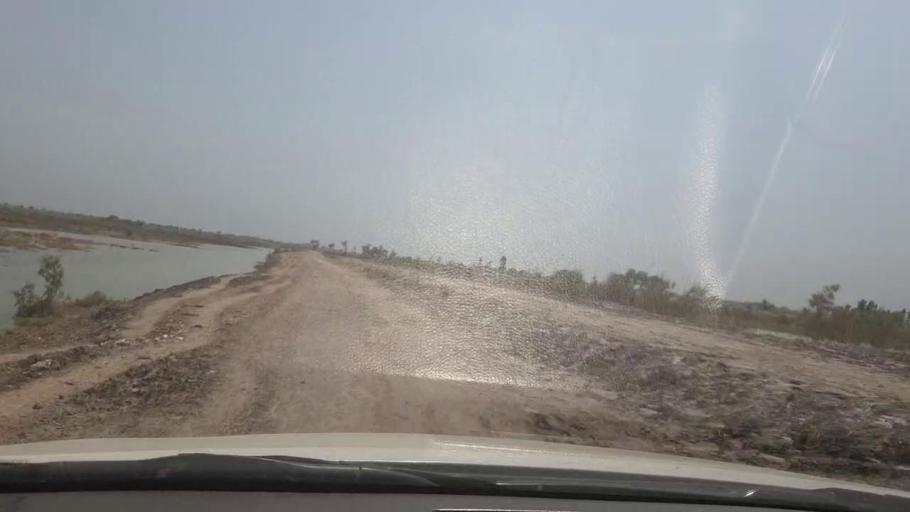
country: PK
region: Sindh
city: Shikarpur
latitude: 28.0350
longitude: 68.5736
